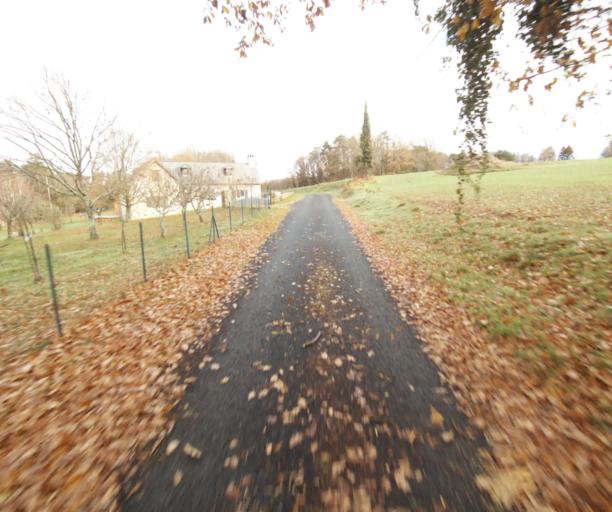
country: FR
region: Limousin
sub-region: Departement de la Correze
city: Saint-Mexant
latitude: 45.2524
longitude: 1.6467
